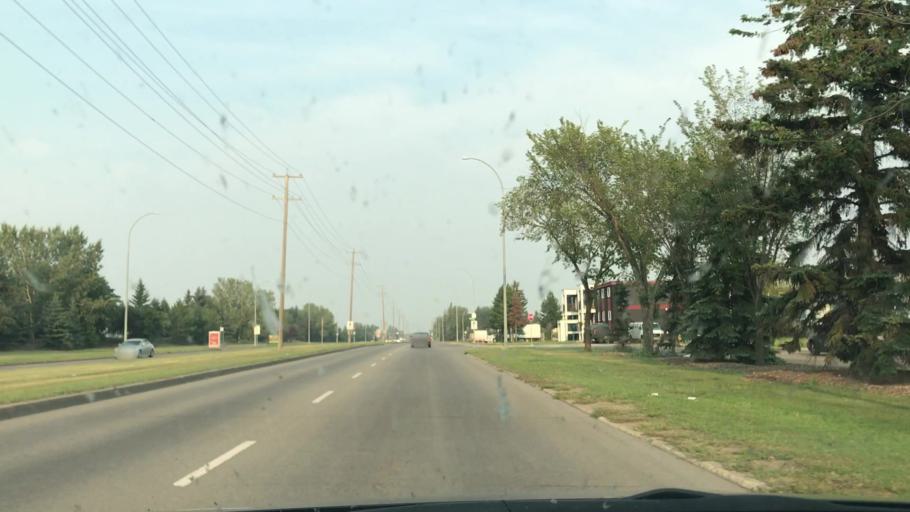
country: CA
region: Alberta
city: Edmonton
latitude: 53.5993
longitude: -113.5291
